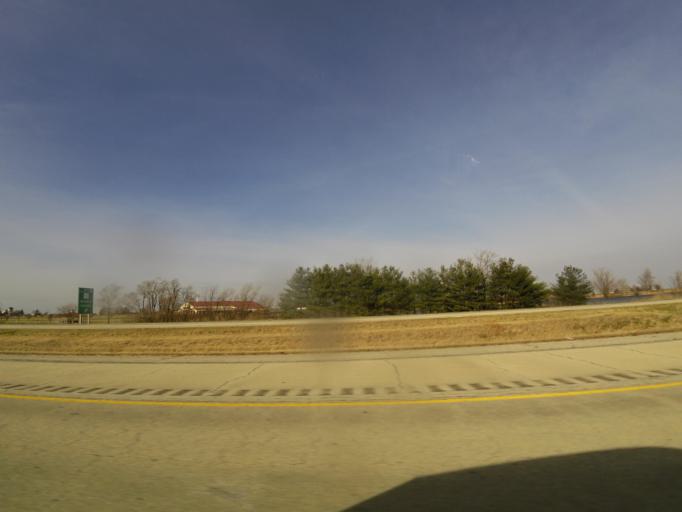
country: US
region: Illinois
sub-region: Macon County
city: Forsyth
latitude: 39.8986
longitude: -89.0009
